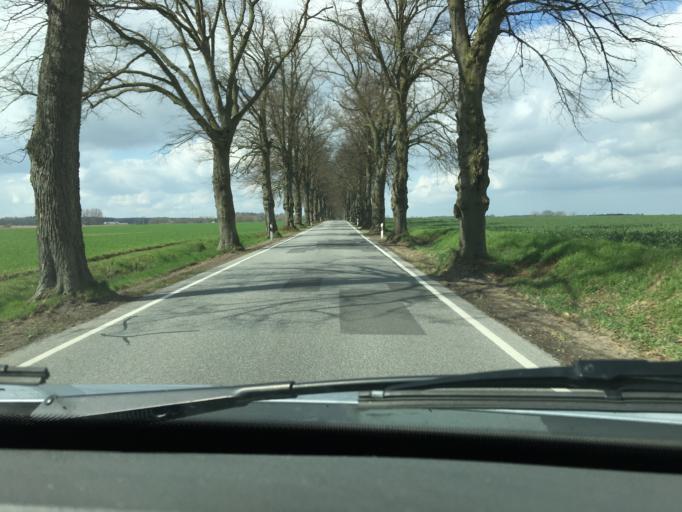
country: DE
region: Mecklenburg-Vorpommern
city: Bad Sulze
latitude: 54.1763
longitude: 12.6401
